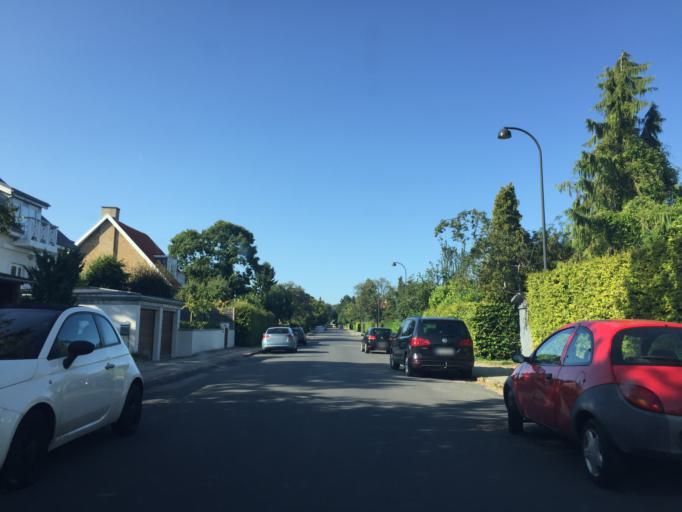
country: DK
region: Capital Region
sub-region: Gentofte Kommune
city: Charlottenlund
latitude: 55.7620
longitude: 12.5569
